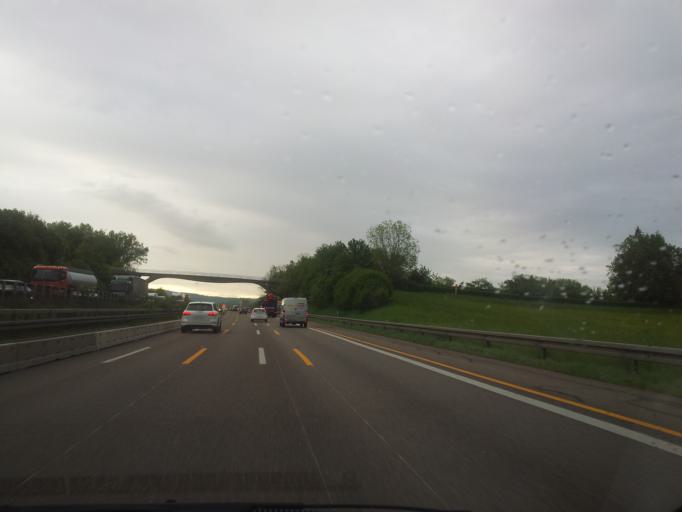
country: DE
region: Baden-Wuerttemberg
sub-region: Regierungsbezirk Stuttgart
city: Kirchheim unter Teck
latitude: 48.6335
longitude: 9.4464
